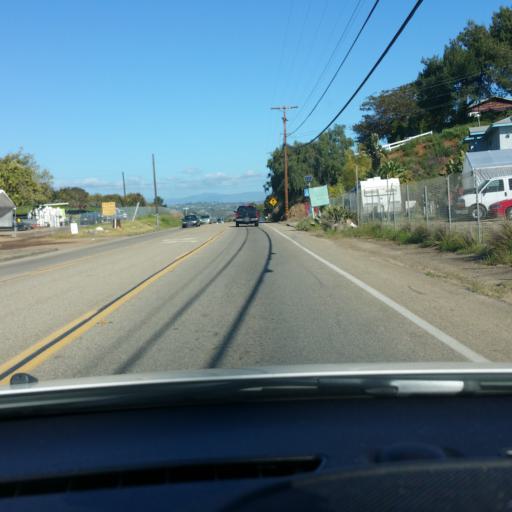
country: US
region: California
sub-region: San Diego County
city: Bonsall
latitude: 33.2435
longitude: -117.2265
